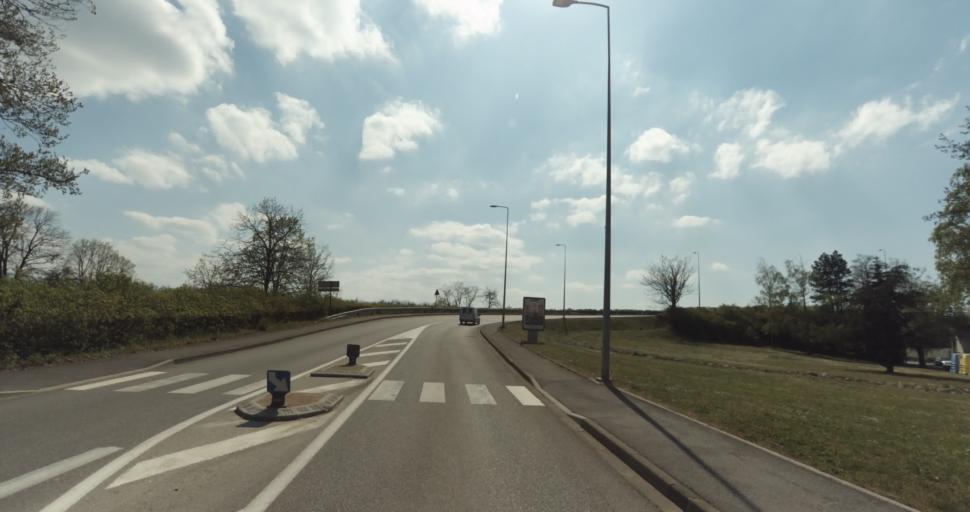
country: FR
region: Rhone-Alpes
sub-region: Departement de l'Isere
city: Saint-Marcellin
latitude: 45.1485
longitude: 5.3193
